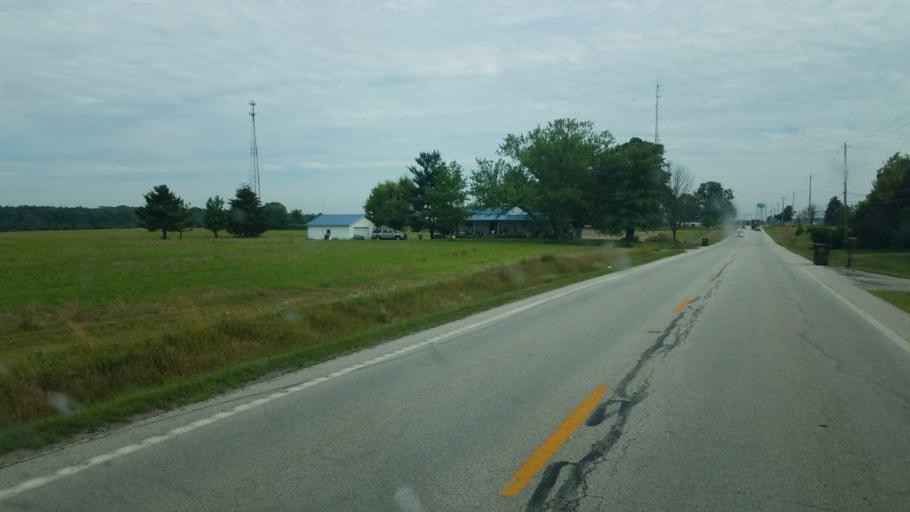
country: US
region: Ohio
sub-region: Lorain County
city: Grafton
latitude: 41.2677
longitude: -82.0222
